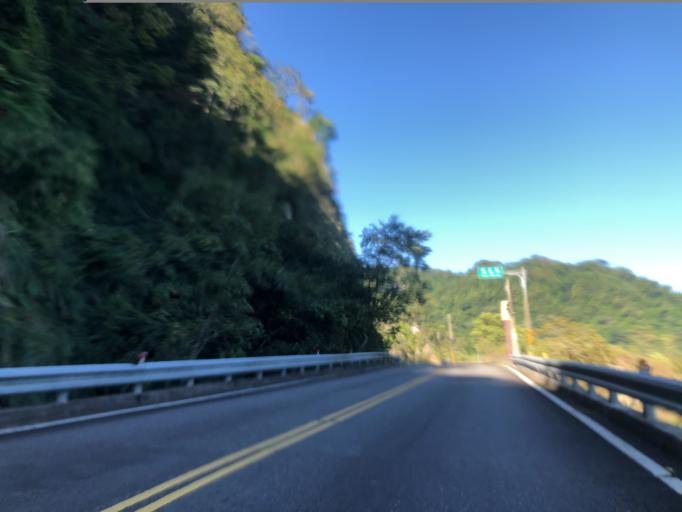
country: TW
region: Taiwan
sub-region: Miaoli
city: Miaoli
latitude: 24.5806
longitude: 120.9335
